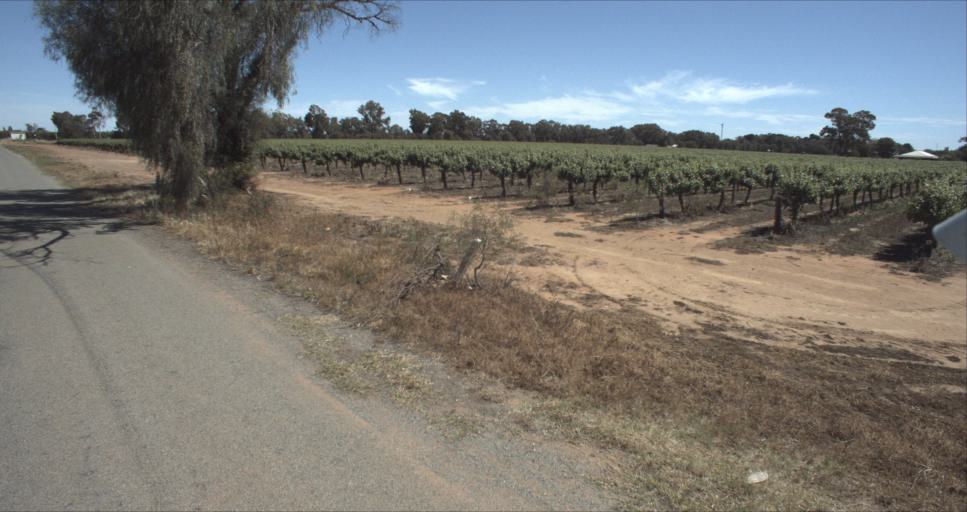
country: AU
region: New South Wales
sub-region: Leeton
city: Leeton
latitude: -34.5295
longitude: 146.3460
